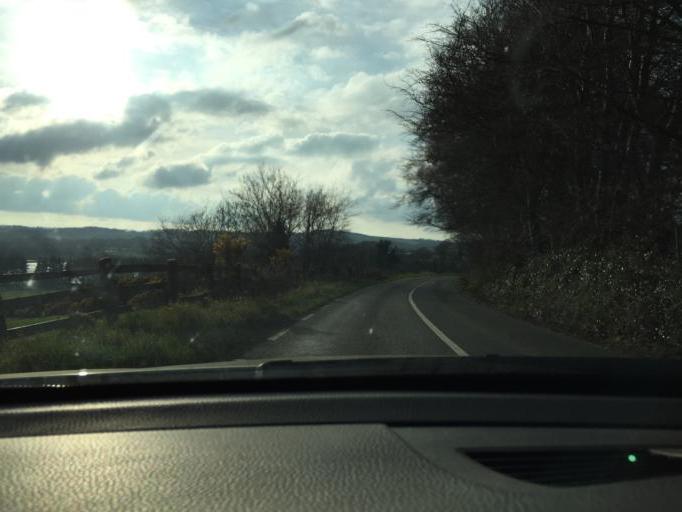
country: IE
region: Leinster
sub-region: Wicklow
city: Blessington
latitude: 53.1619
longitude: -6.5186
